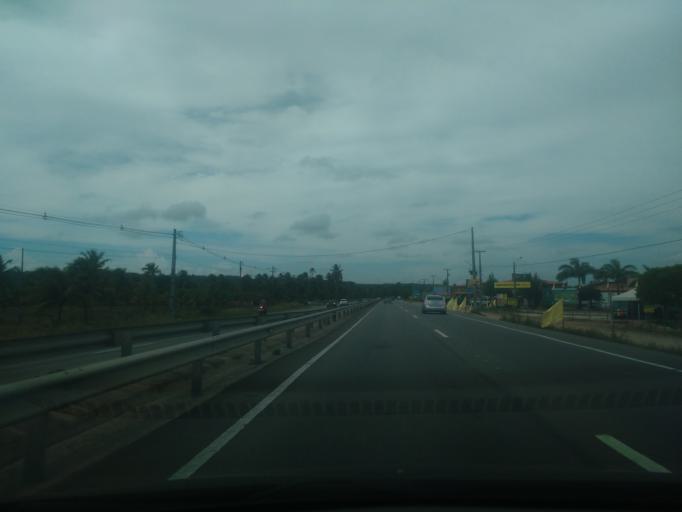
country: BR
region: Alagoas
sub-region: Marechal Deodoro
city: Marechal Deodoro
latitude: -9.7182
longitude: -35.8265
